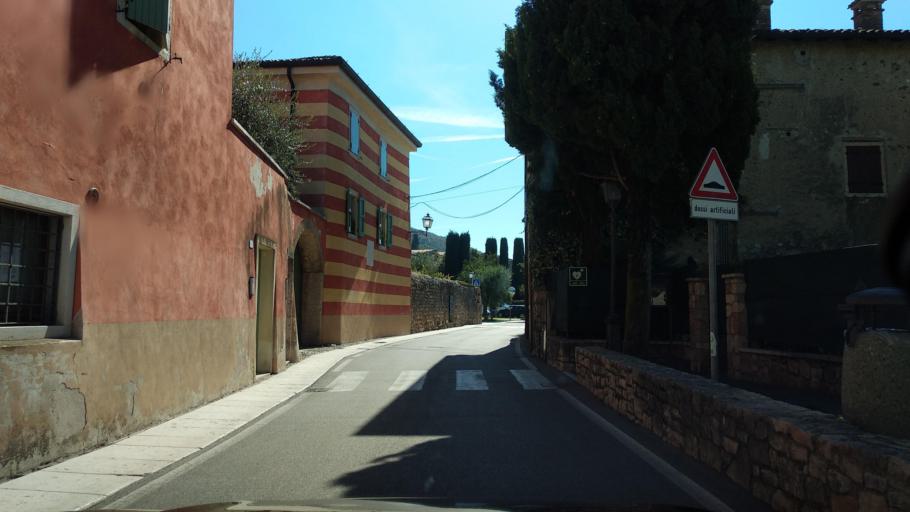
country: IT
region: Veneto
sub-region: Provincia di Verona
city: Torri del Benaco
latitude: 45.6112
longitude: 10.7020
